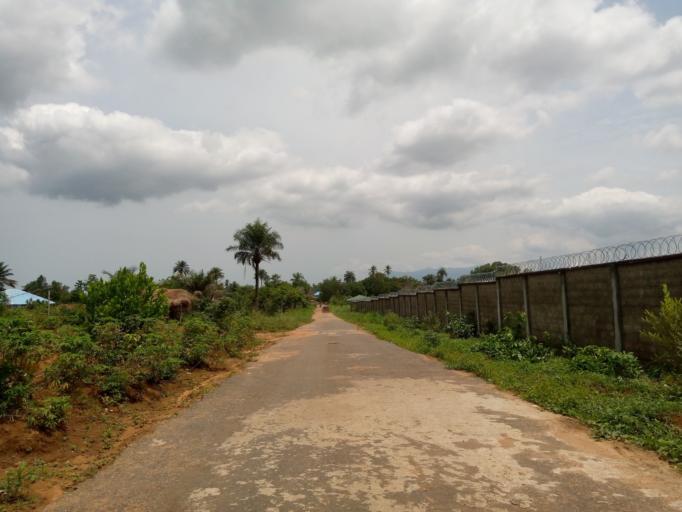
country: SL
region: Western Area
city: Waterloo
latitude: 8.3510
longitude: -12.9809
